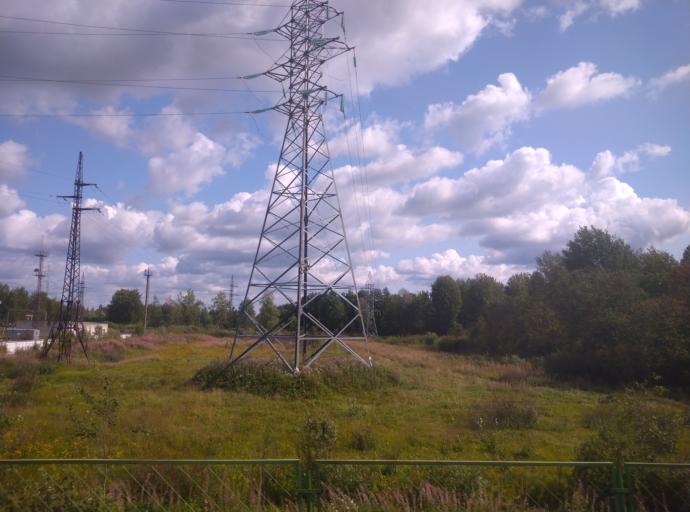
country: RU
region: Leningrad
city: Krasnyy Bor
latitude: 59.6754
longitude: 30.7085
